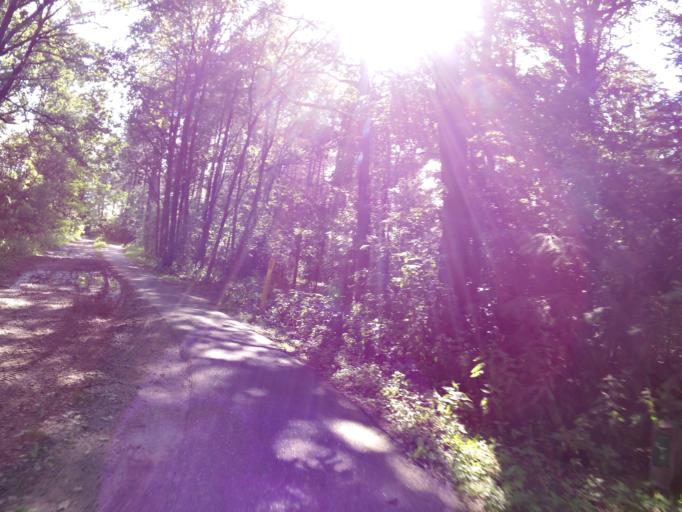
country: NL
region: North Brabant
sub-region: Gemeente Geldrop-Mierlo
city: Geldrop
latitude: 51.4033
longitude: 5.5297
